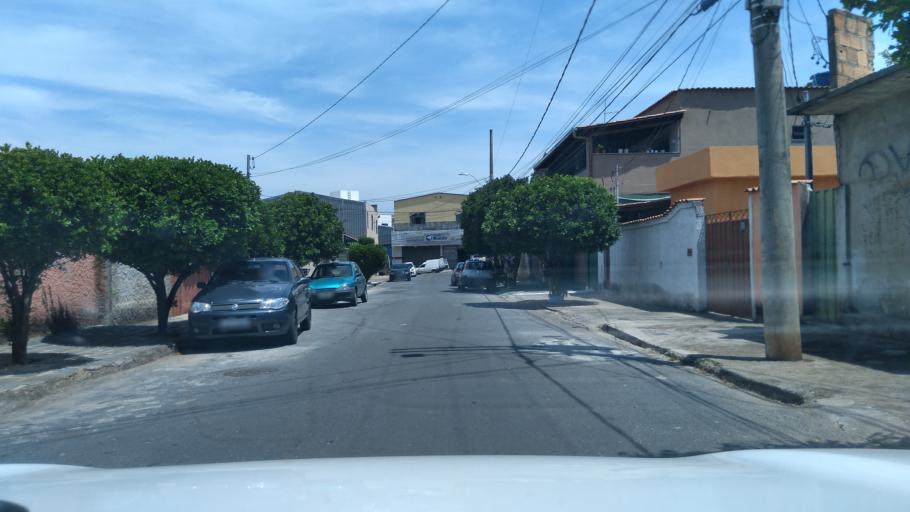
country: BR
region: Minas Gerais
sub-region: Contagem
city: Contagem
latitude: -19.9034
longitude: -44.0178
